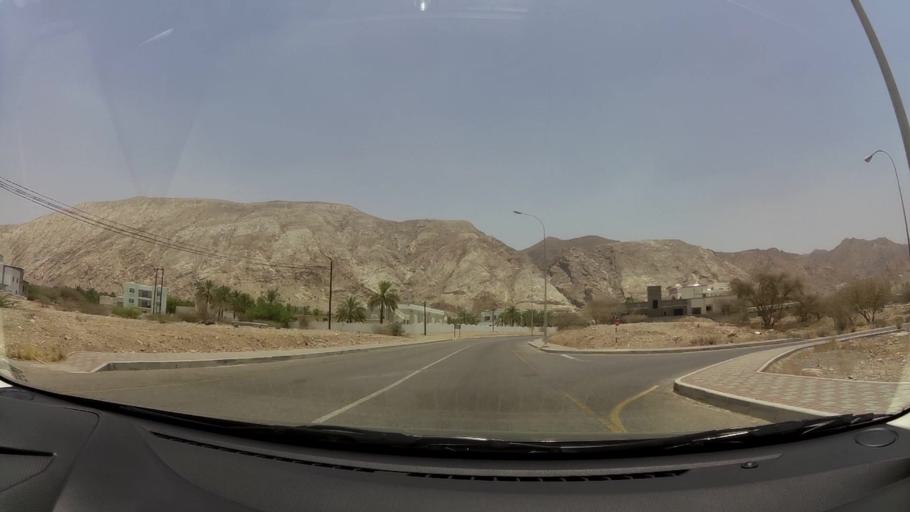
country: OM
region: Muhafazat Masqat
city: Bawshar
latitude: 23.5539
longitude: 58.4092
